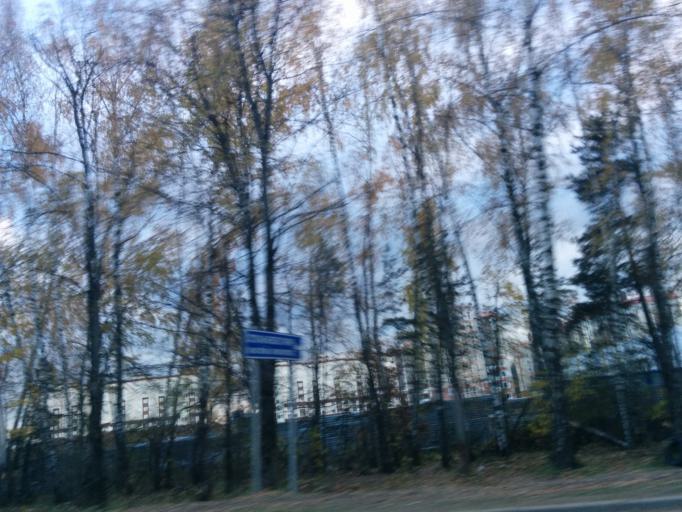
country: RU
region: Moscow
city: Zagor'ye
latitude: 55.5381
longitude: 37.6367
